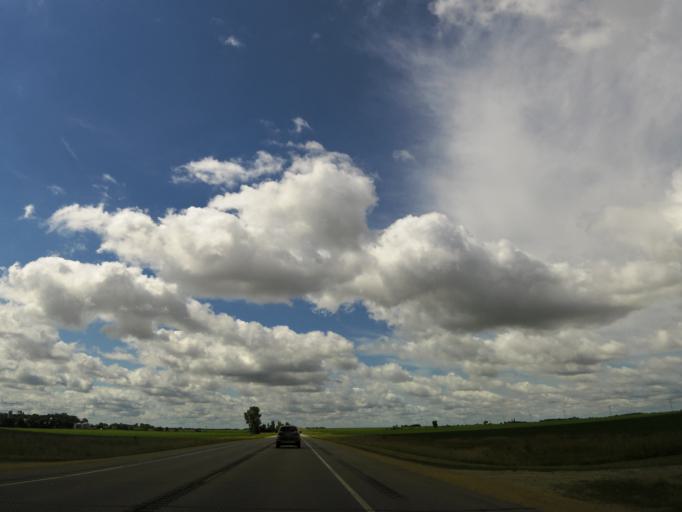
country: US
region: Minnesota
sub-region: Olmsted County
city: Stewartville
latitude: 43.8125
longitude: -92.4897
